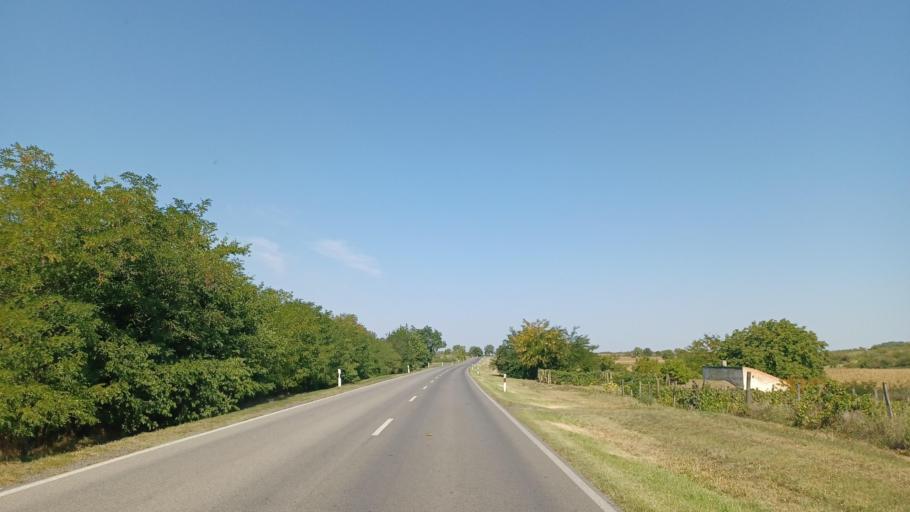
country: HU
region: Tolna
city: Nagydorog
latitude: 46.6392
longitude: 18.6512
